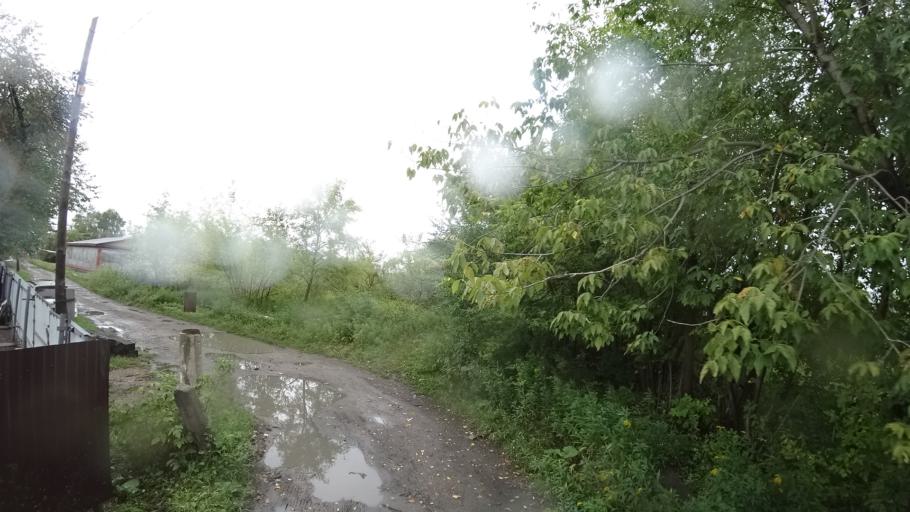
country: RU
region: Primorskiy
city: Monastyrishche
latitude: 44.1964
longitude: 132.4236
